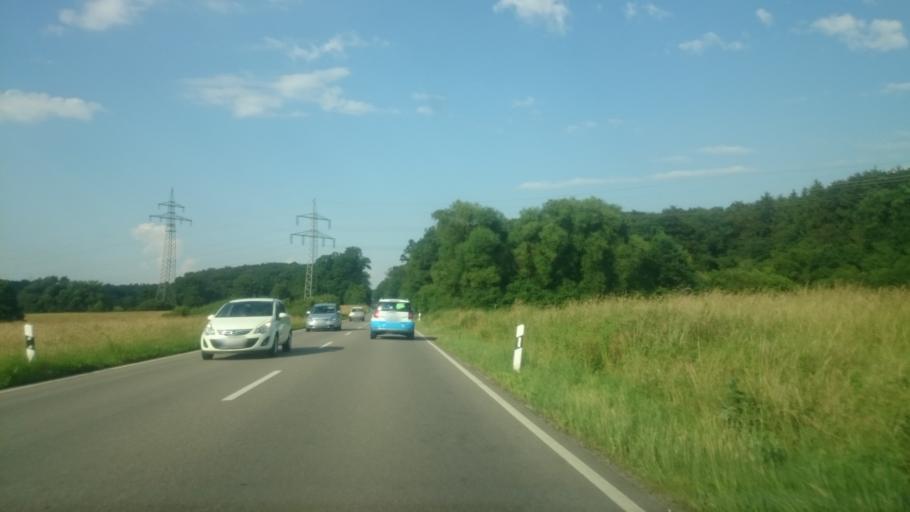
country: DE
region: Baden-Wuerttemberg
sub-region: Tuebingen Region
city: Gomaringen
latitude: 48.4652
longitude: 9.1137
